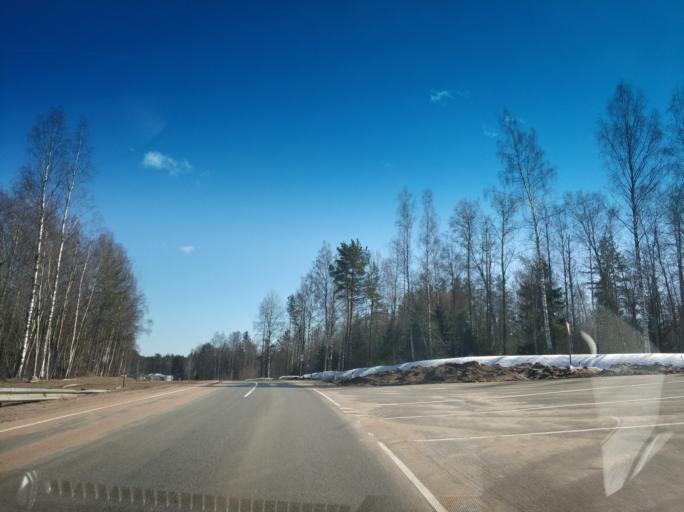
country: RU
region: Leningrad
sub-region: Vsevolzhskij Rajon
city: Vaskelovo
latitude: 60.4264
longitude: 30.2471
